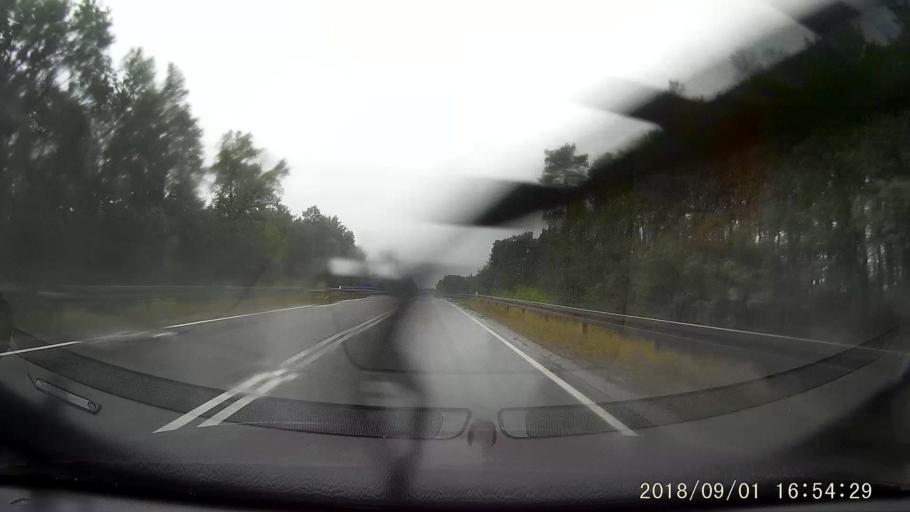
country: PL
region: Lubusz
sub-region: Zielona Gora
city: Zielona Gora
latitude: 51.9571
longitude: 15.4544
